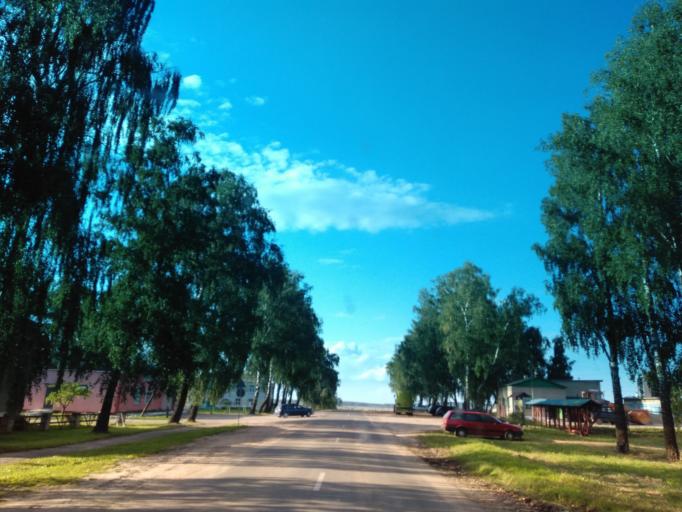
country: BY
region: Minsk
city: Kapyl'
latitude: 53.2623
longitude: 26.9575
